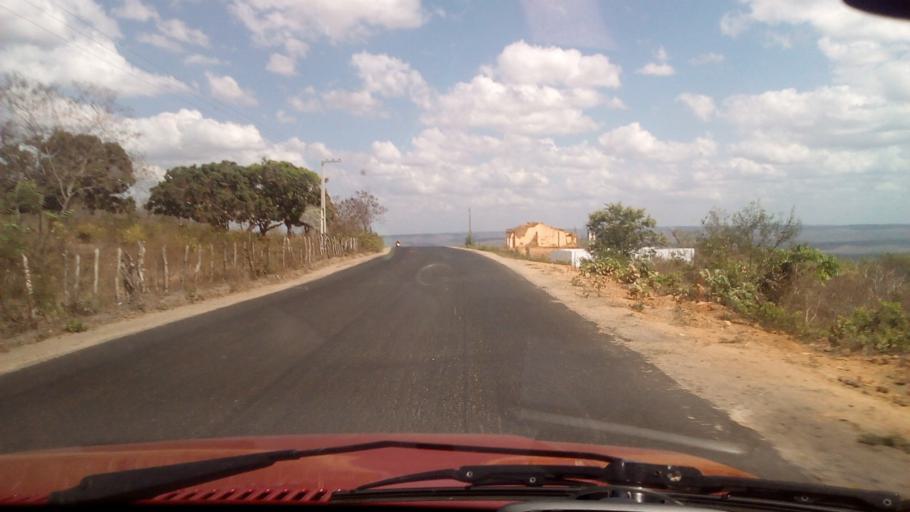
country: BR
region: Paraiba
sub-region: Cacimba De Dentro
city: Cacimba de Dentro
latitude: -6.6491
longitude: -35.7819
